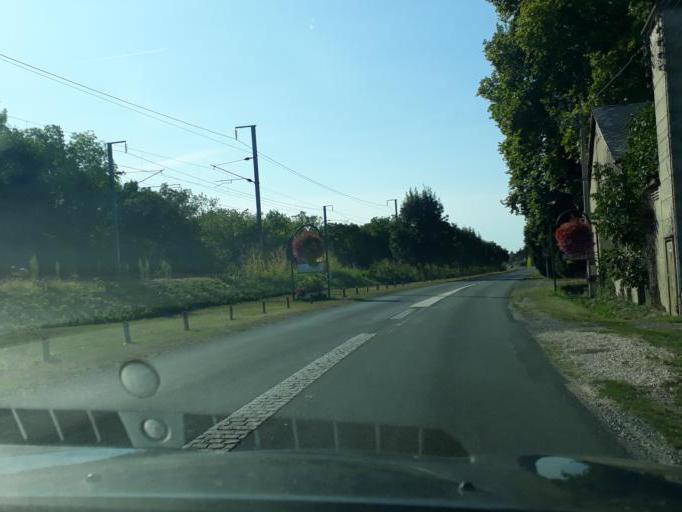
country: FR
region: Centre
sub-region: Departement du Loir-et-Cher
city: Thesee
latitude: 47.3271
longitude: 1.3002
